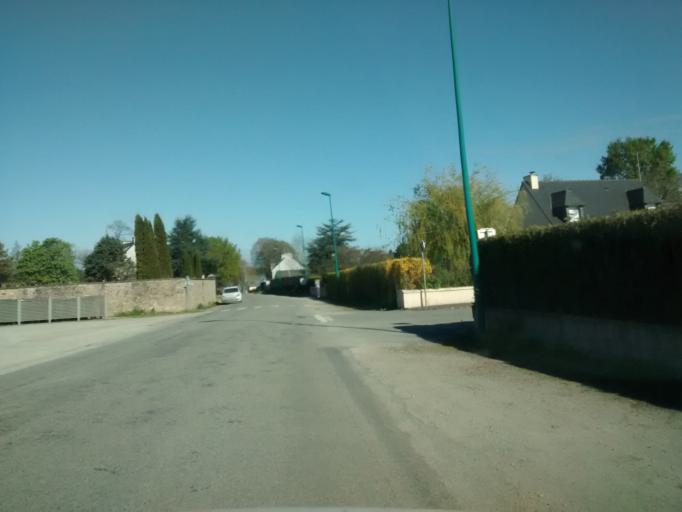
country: FR
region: Brittany
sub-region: Departement du Morbihan
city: Malestroit
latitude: 47.8638
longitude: -2.4187
